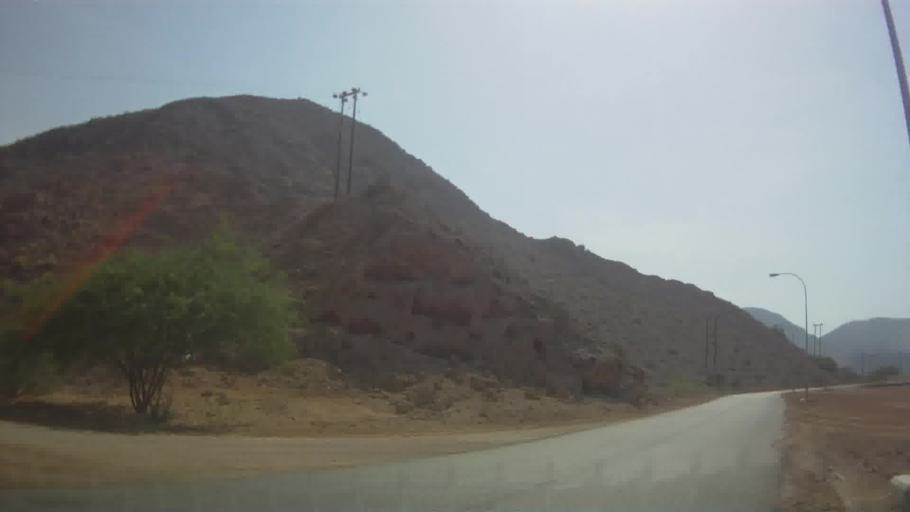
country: OM
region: Muhafazat Masqat
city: Muscat
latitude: 23.5115
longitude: 58.7394
